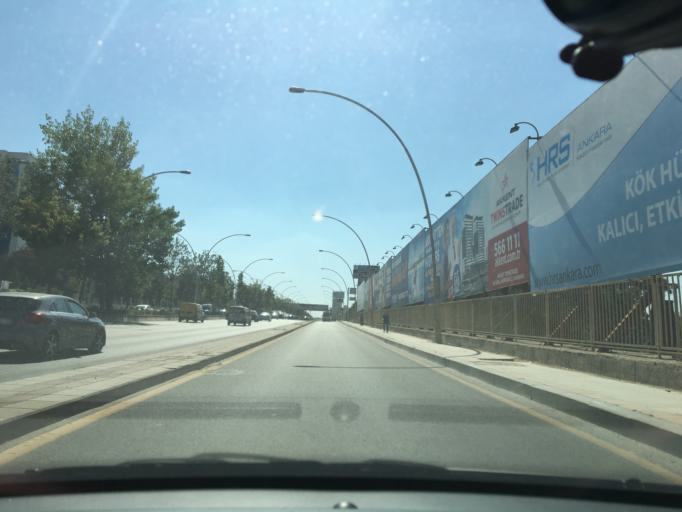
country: TR
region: Ankara
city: Batikent
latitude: 39.9073
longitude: 32.7483
